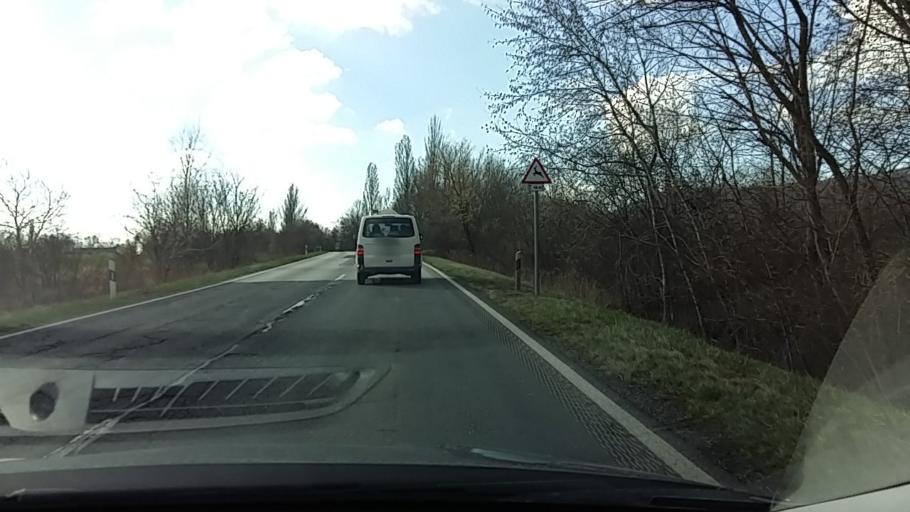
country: HU
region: Veszprem
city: Tapolca
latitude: 46.8403
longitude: 17.3713
